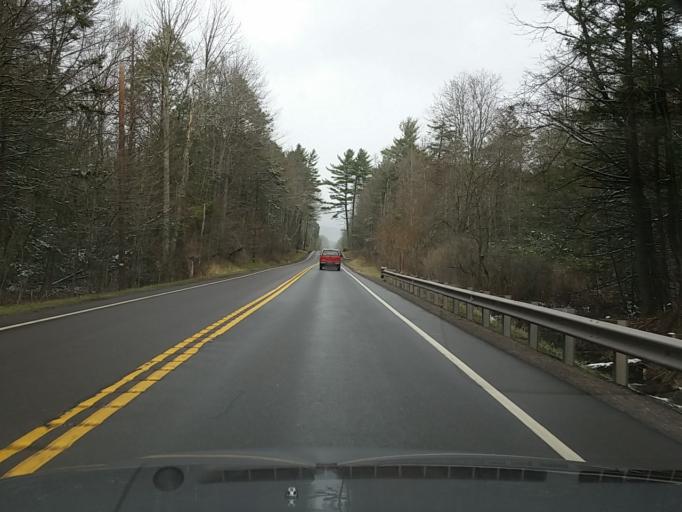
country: US
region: Pennsylvania
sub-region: Sullivan County
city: Laporte
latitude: 41.2905
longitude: -76.2966
